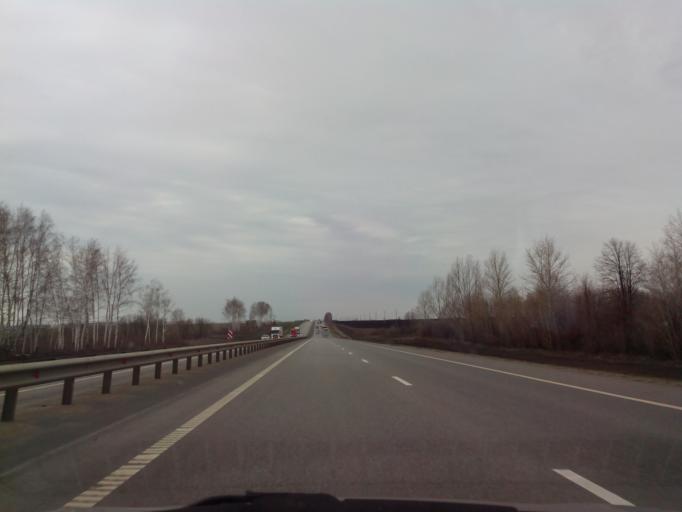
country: RU
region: Tambov
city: Selezni
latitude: 52.8121
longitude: 40.9509
